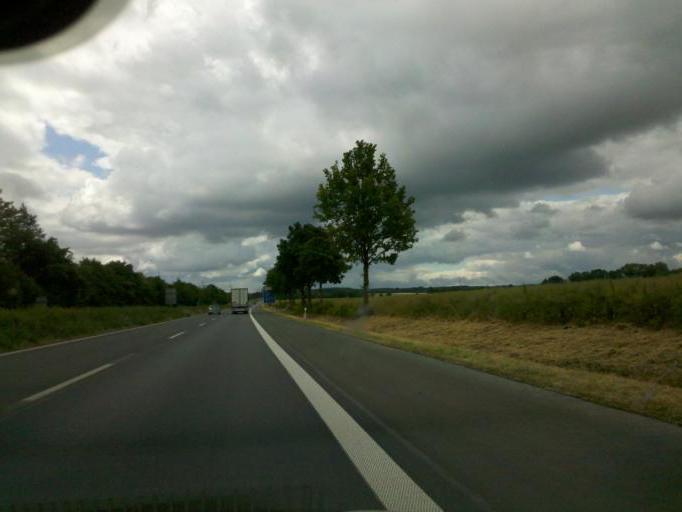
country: DE
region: North Rhine-Westphalia
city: Erwitte
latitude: 51.5998
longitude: 8.3118
